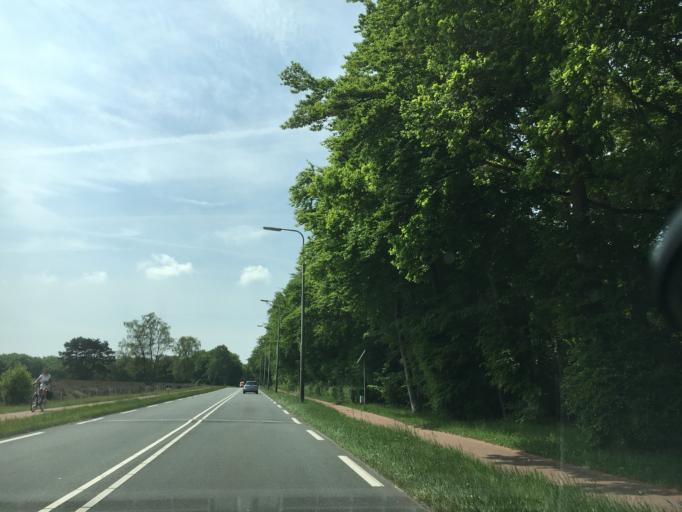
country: NL
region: North Holland
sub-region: Gemeente Laren
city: Laren
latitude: 52.2811
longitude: 5.2137
